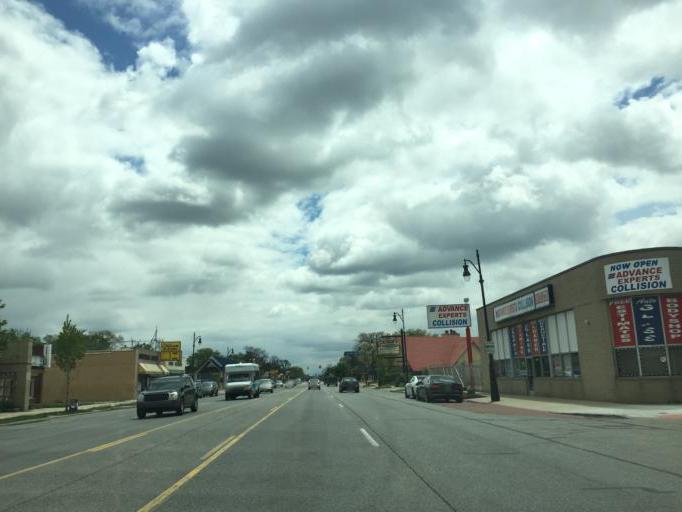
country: US
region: Michigan
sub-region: Wayne County
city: Redford
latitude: 42.4075
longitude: -83.2353
